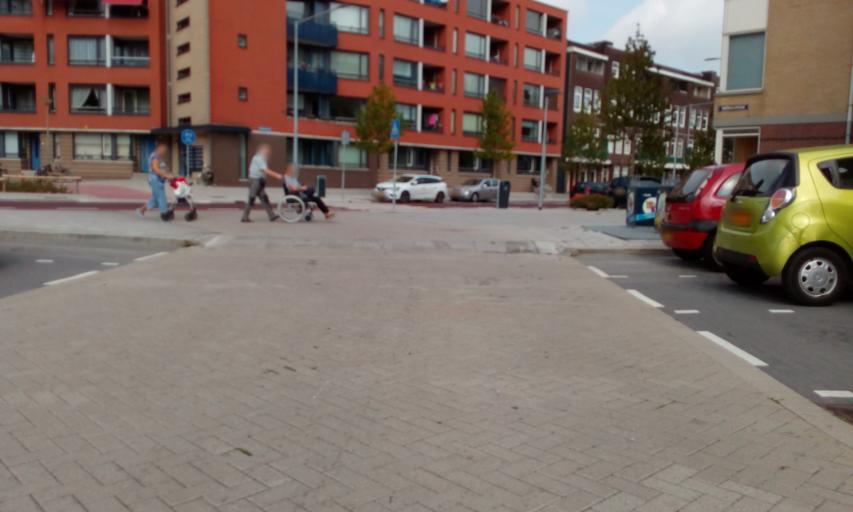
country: NL
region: South Holland
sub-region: Gemeente Schiedam
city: Schiedam
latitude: 51.9149
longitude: 4.4121
